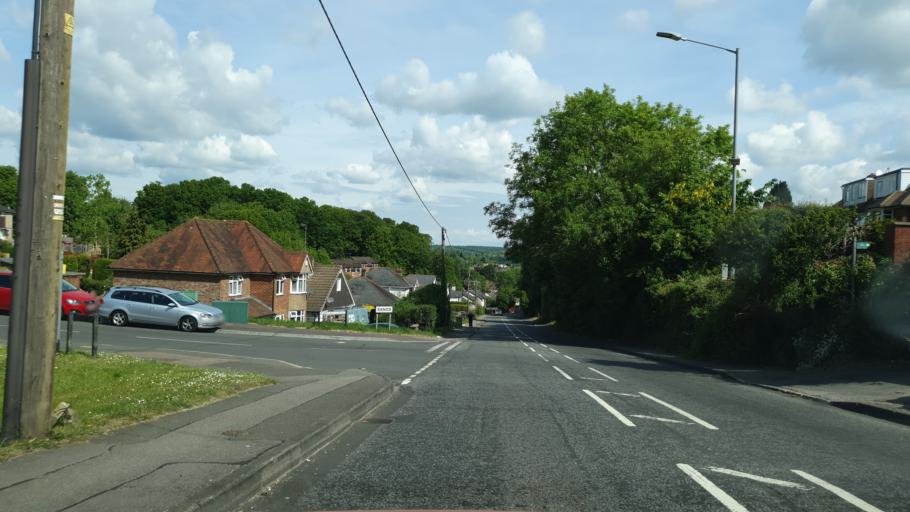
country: GB
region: England
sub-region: Buckinghamshire
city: High Wycombe
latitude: 51.6227
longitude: -0.7850
